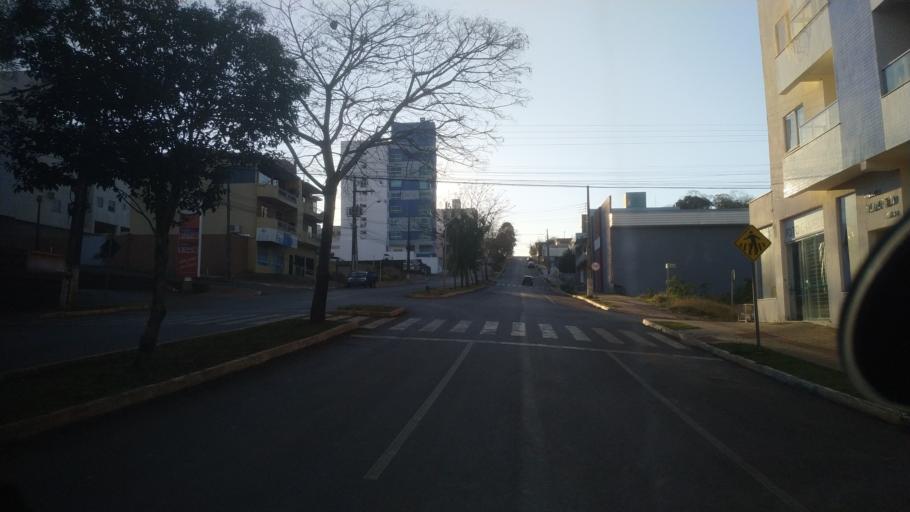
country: BR
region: Santa Catarina
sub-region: Chapeco
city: Chapeco
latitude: -27.0895
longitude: -52.5904
